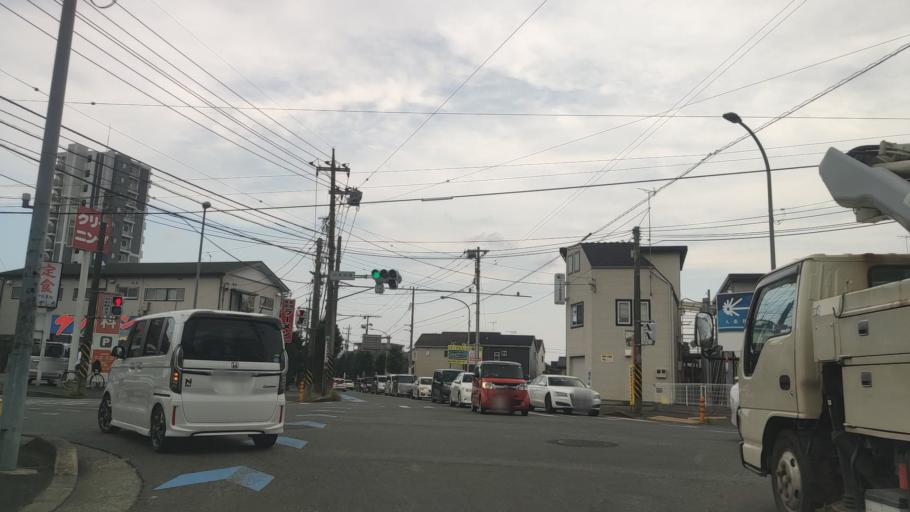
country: JP
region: Kanagawa
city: Minami-rinkan
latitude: 35.5014
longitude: 139.4498
